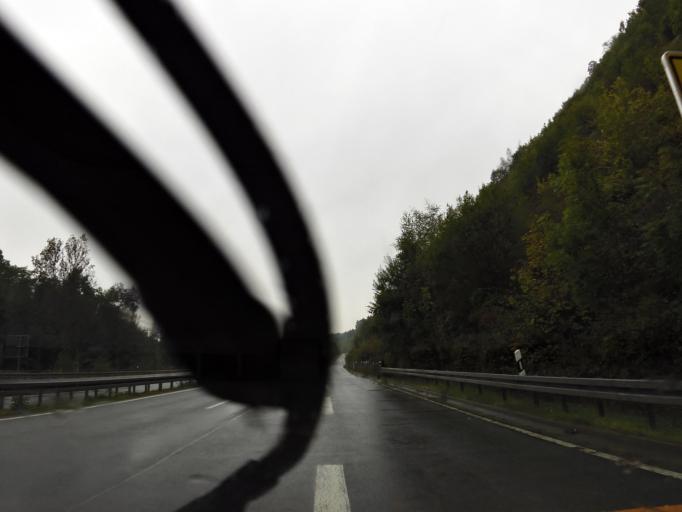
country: DE
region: Lower Saxony
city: Bad Lauterberg im Harz
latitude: 51.6254
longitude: 10.4246
